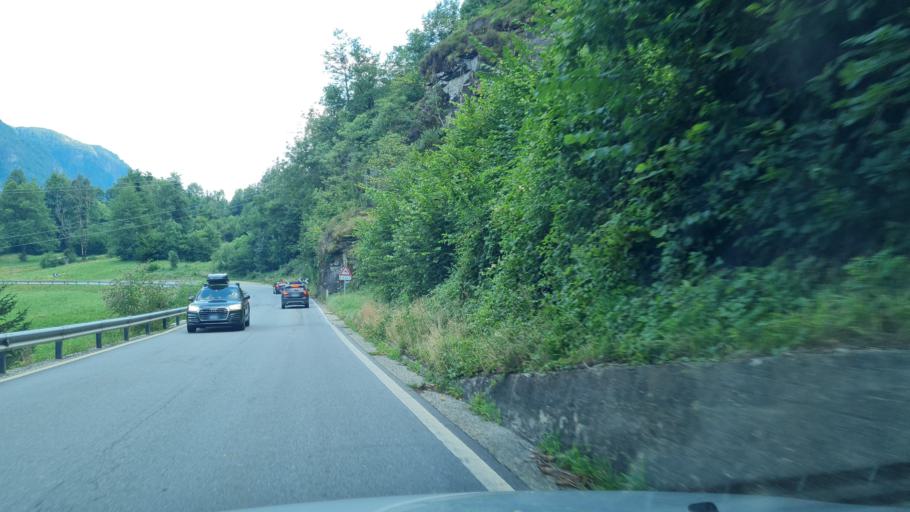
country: IT
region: Piedmont
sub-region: Provincia Verbano-Cusio-Ossola
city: Crodo
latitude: 46.2344
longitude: 8.3211
